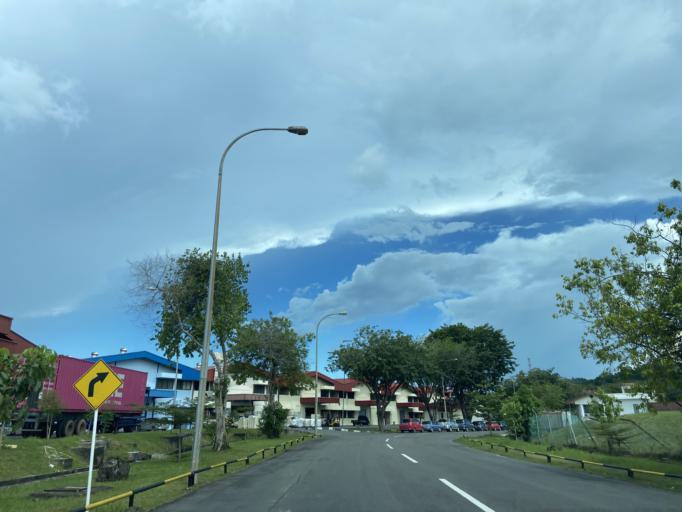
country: SG
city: Singapore
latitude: 1.0604
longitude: 104.0304
